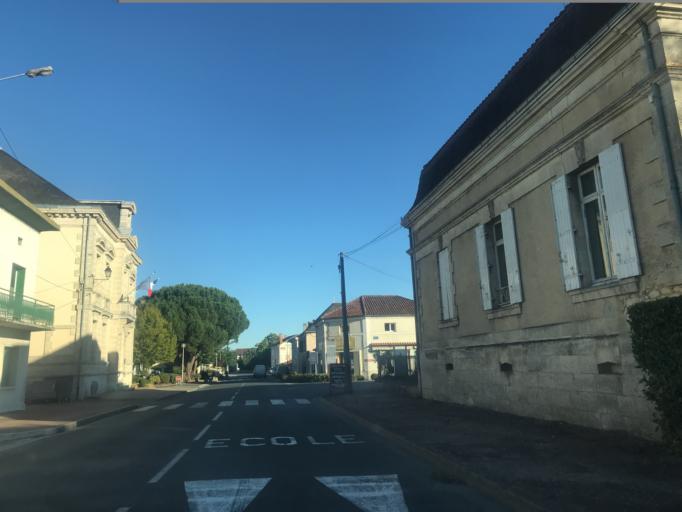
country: FR
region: Poitou-Charentes
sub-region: Departement de la Charente-Maritime
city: Saint-Aigulin
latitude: 45.1600
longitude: -0.0182
